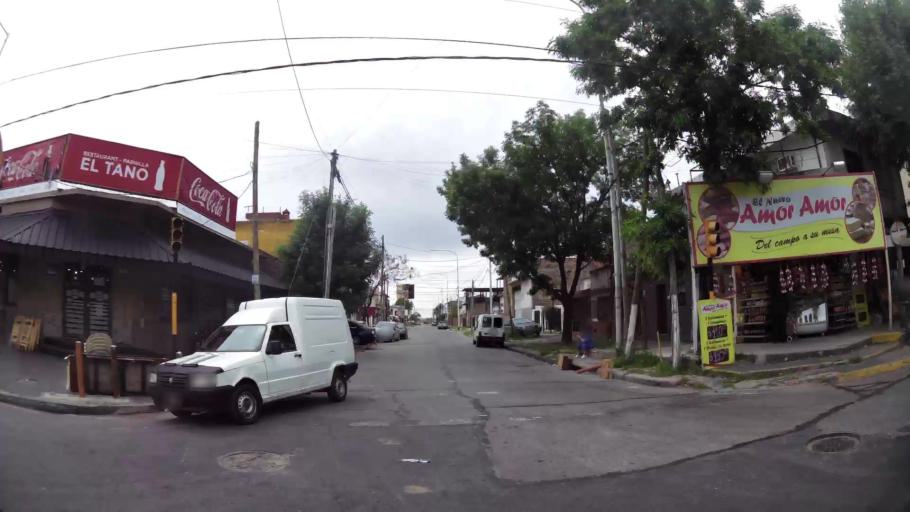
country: AR
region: Buenos Aires
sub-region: Partido de Avellaneda
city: Avellaneda
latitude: -34.6695
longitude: -58.3435
